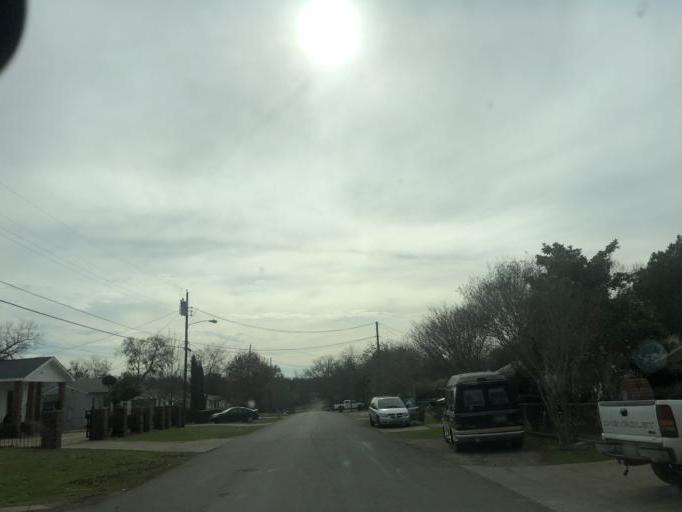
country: US
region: Texas
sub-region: Dallas County
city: Duncanville
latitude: 32.6689
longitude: -96.8338
